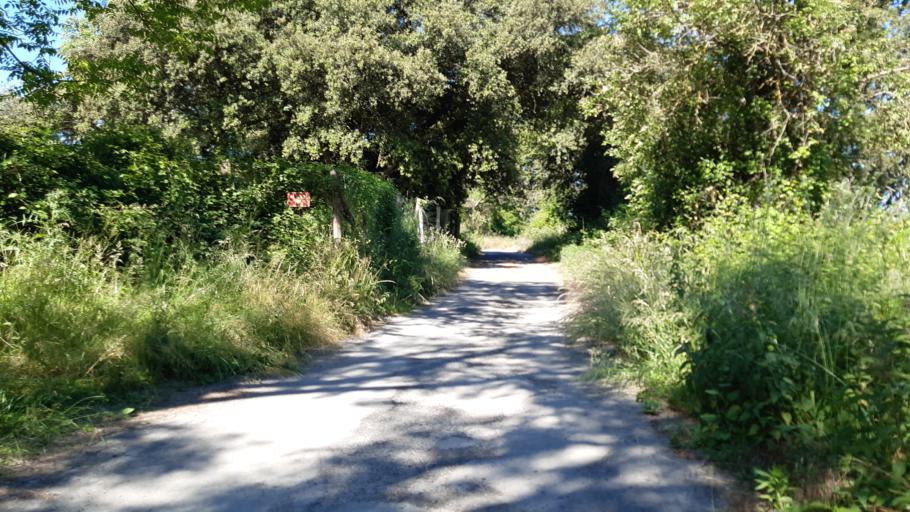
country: FR
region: Centre
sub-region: Departement d'Indre-et-Loire
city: Mettray
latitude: 47.4345
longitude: 0.6596
